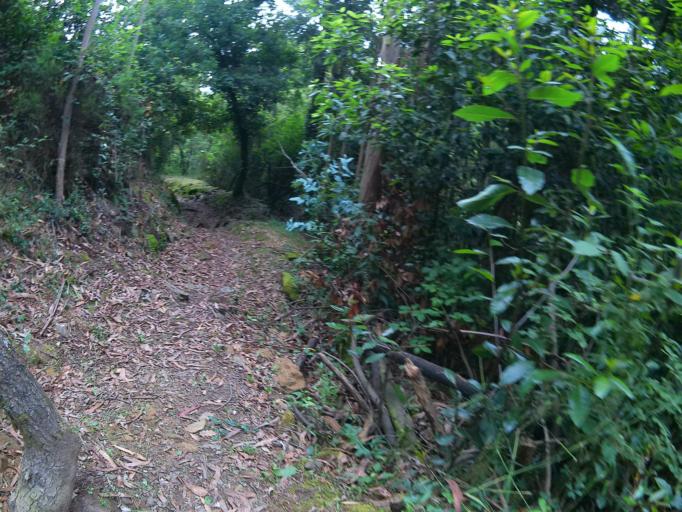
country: PT
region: Aveiro
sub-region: Albergaria-A-Velha
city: Branca
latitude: 40.7512
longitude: -8.4298
